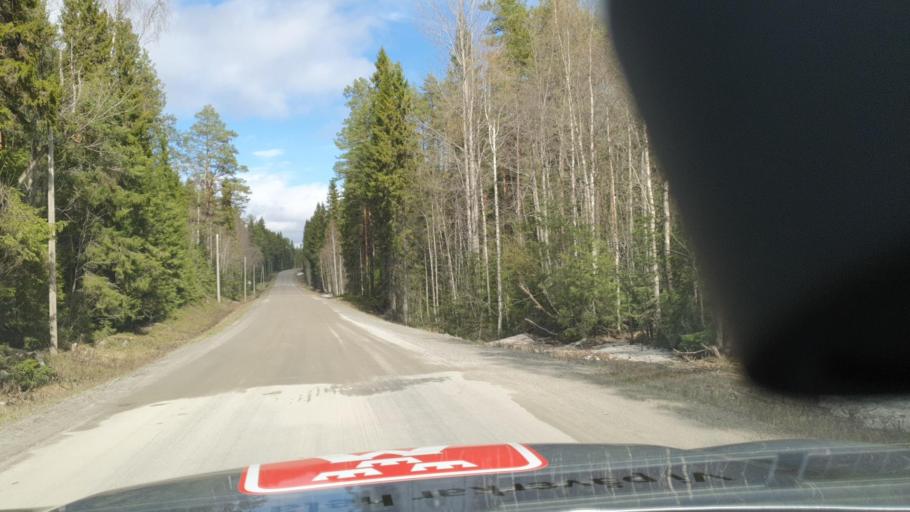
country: SE
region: Vaesterbotten
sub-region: Bjurholms Kommun
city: Bjurholm
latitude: 63.6977
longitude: 18.8959
